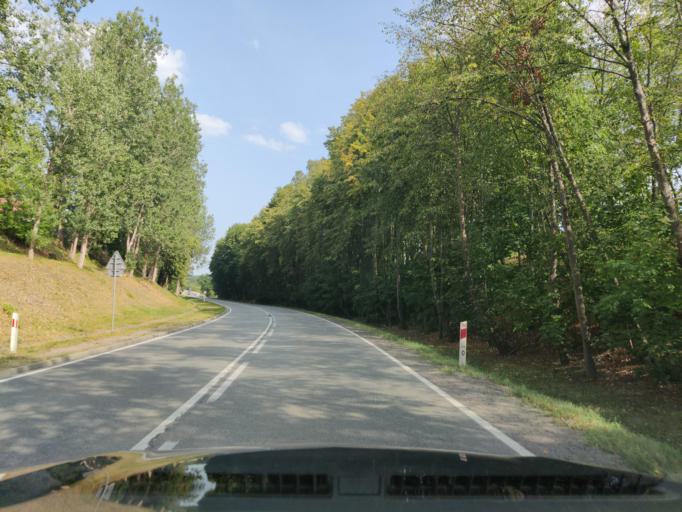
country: PL
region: Masovian Voivodeship
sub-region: Powiat makowski
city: Rozan
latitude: 52.8845
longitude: 21.3992
